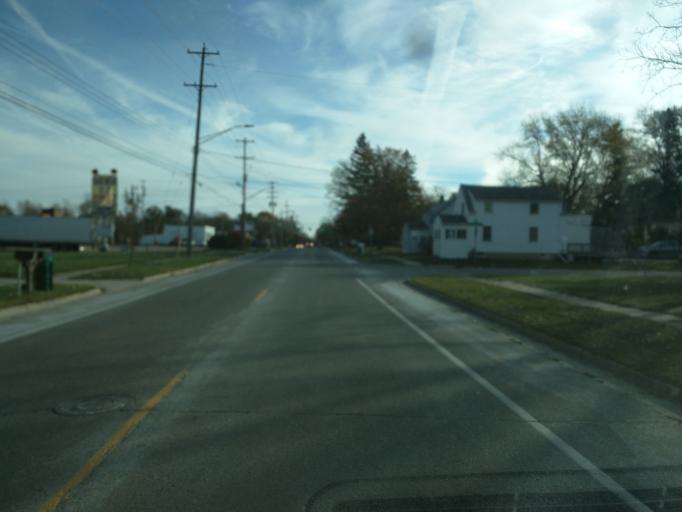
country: US
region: Michigan
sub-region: Ingham County
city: Holt
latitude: 42.6693
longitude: -84.5650
